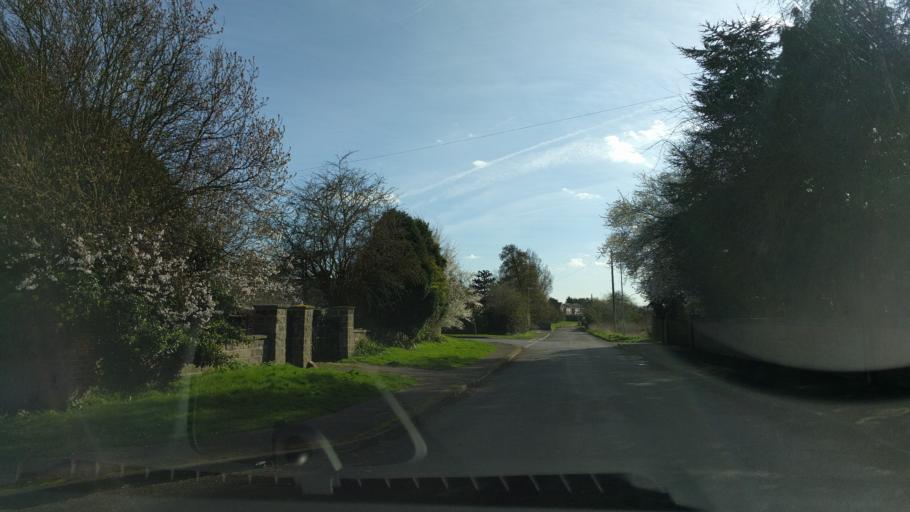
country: GB
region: England
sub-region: Cambridgeshire
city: Chatteris
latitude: 52.4481
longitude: 0.0400
